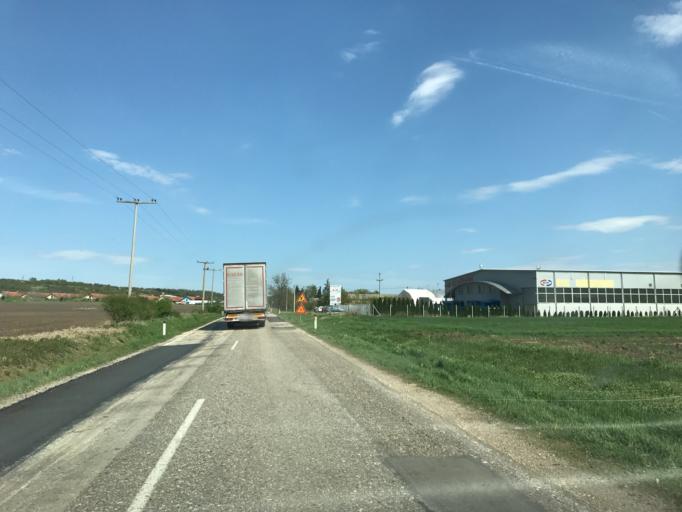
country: RS
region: Central Serbia
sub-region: Zajecarski Okrug
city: Zajecar
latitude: 43.9061
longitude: 22.2367
